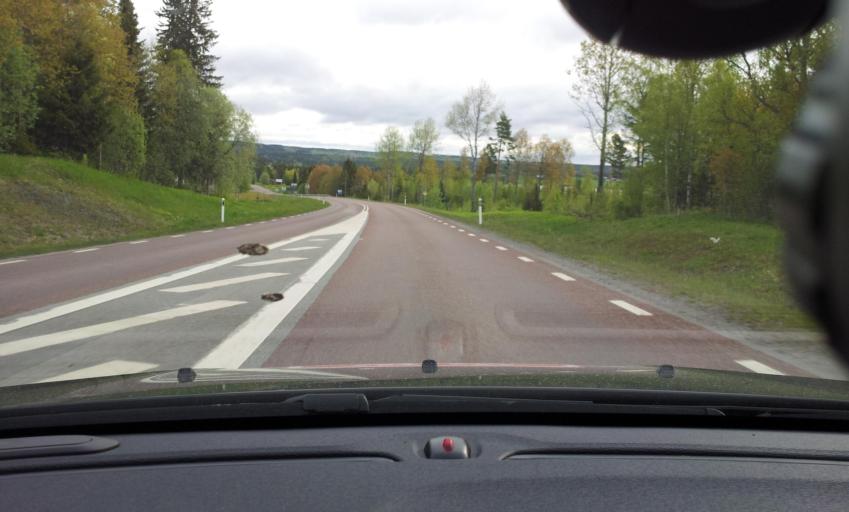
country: SE
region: Jaemtland
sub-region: OEstersunds Kommun
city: Brunflo
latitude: 63.0377
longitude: 14.8116
